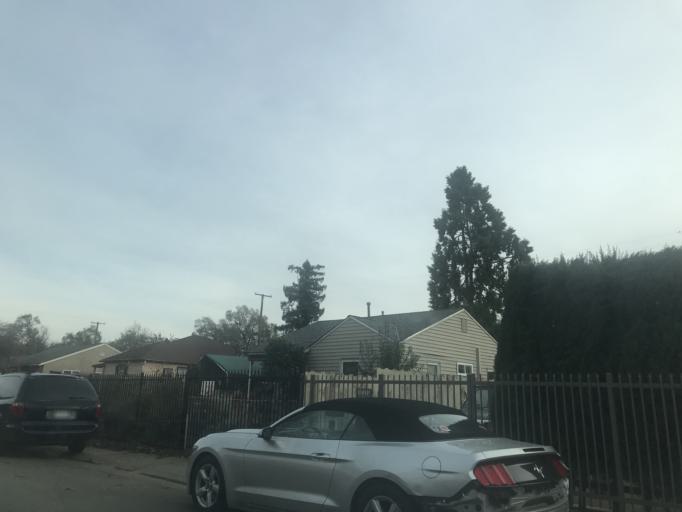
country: US
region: California
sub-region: Sacramento County
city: Parkway
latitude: 38.5216
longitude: -121.4746
